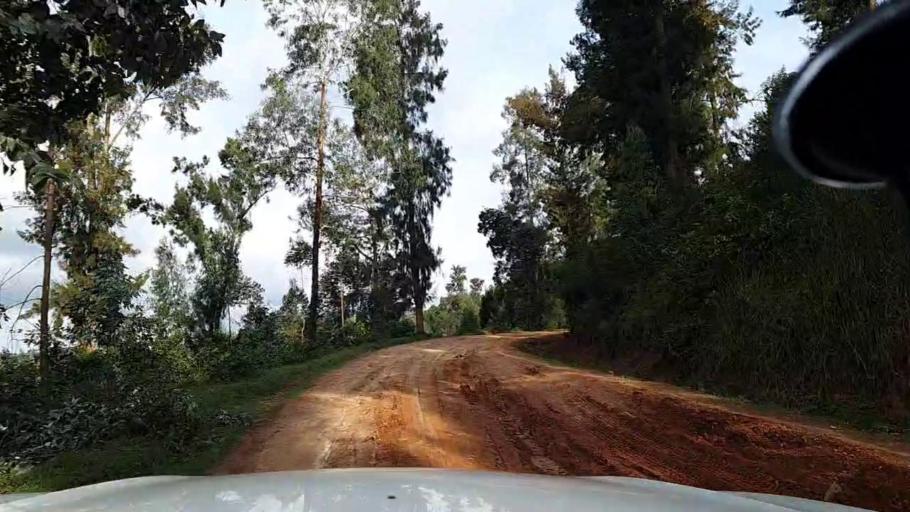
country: RW
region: Southern Province
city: Gitarama
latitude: -2.1631
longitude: 29.5530
